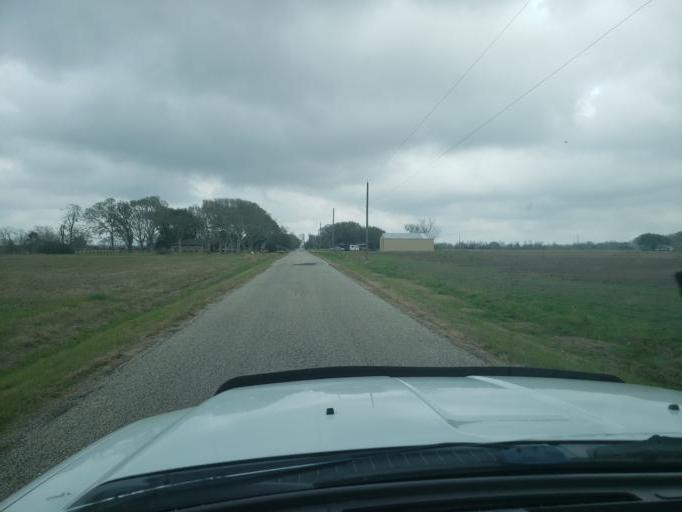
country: US
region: Texas
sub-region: Fort Bend County
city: Needville
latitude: 29.3410
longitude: -95.7638
